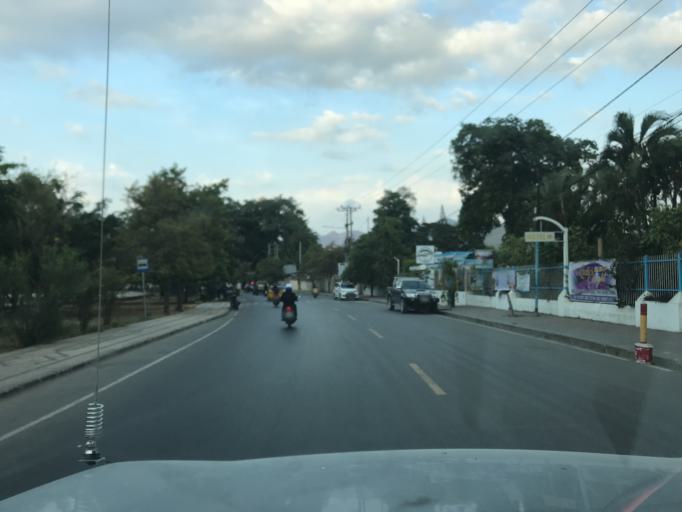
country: TL
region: Dili
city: Dili
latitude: -8.5519
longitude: 125.5822
